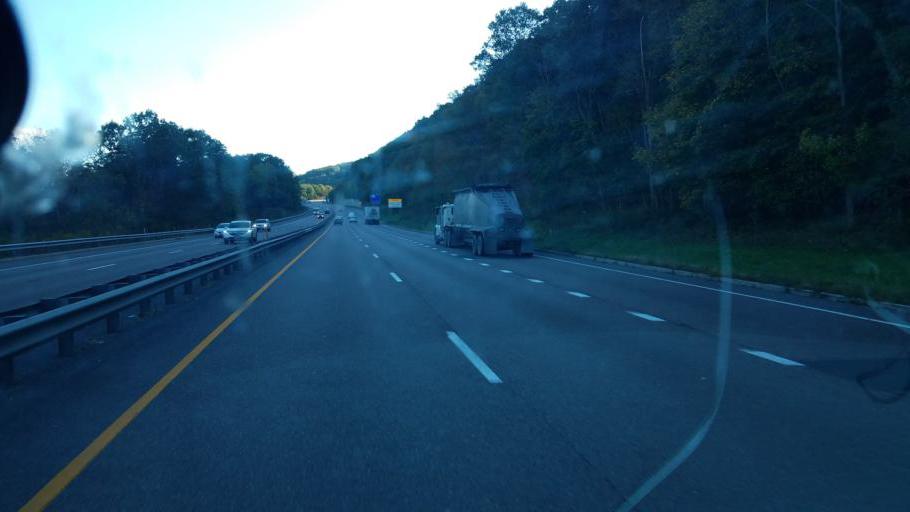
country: US
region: Maryland
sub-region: Allegany County
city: La Vale
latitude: 39.6372
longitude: -78.8221
